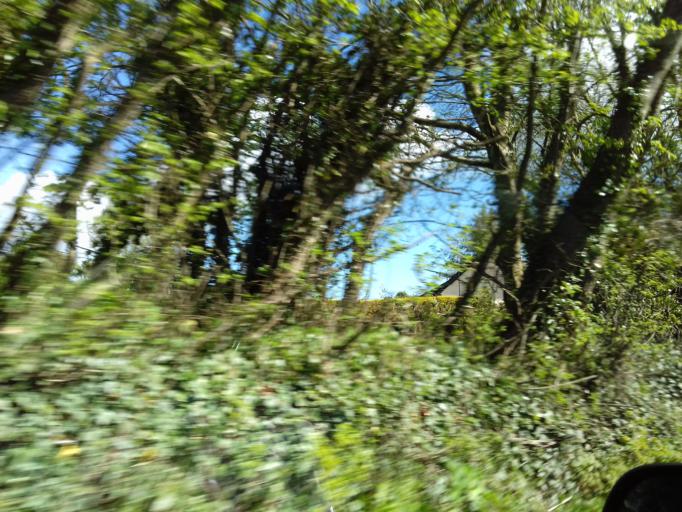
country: IE
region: Leinster
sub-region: Loch Garman
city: Castlebridge
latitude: 52.3926
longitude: -6.3975
